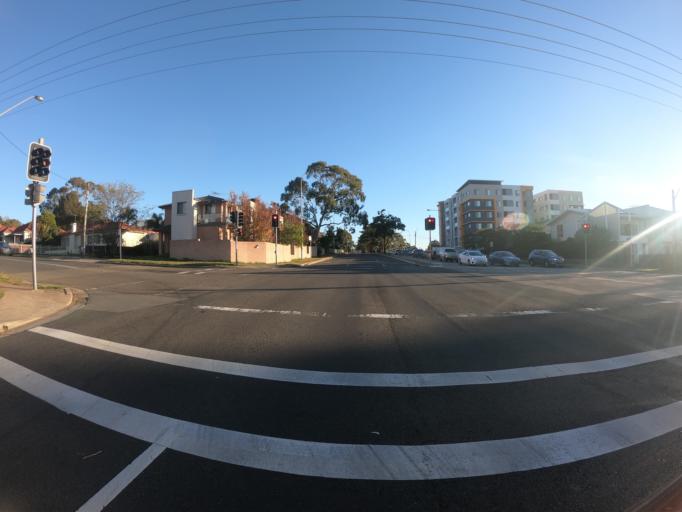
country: AU
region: New South Wales
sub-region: Campbelltown Municipality
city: Campbelltown
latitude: -34.0643
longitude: 150.8237
